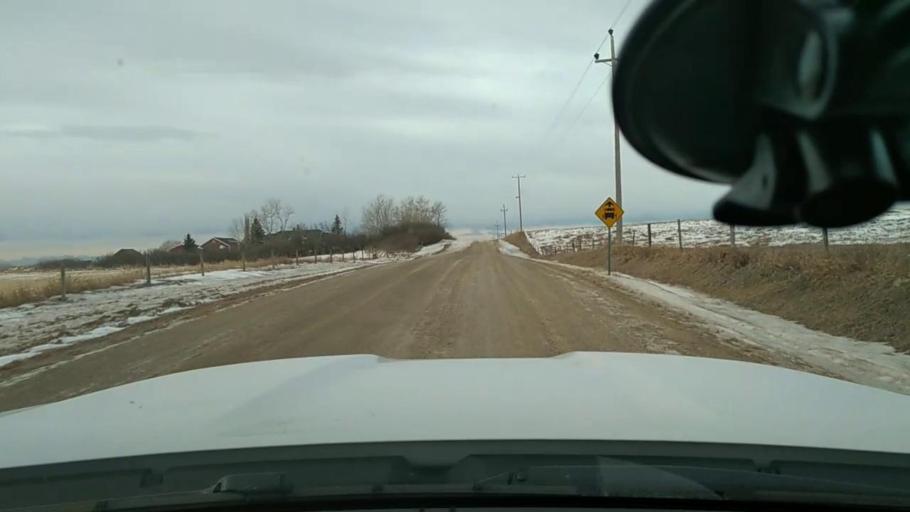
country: CA
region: Alberta
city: Airdrie
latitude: 51.2417
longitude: -113.9176
